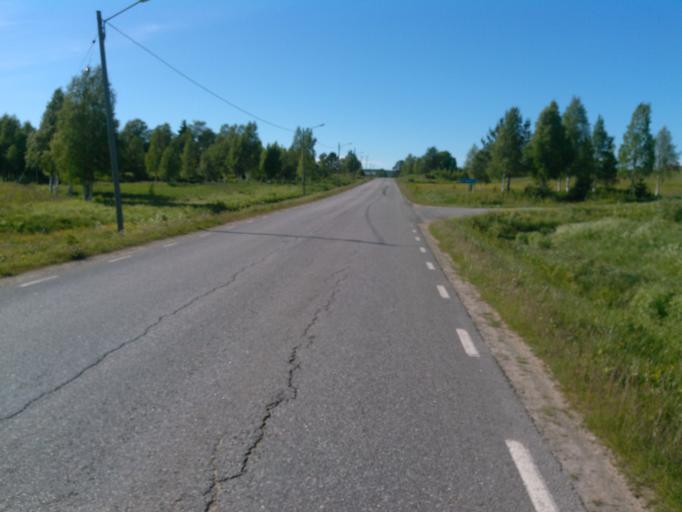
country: SE
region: Vaesterbotten
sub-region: Umea Kommun
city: Roback
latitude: 63.8251
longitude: 20.1233
